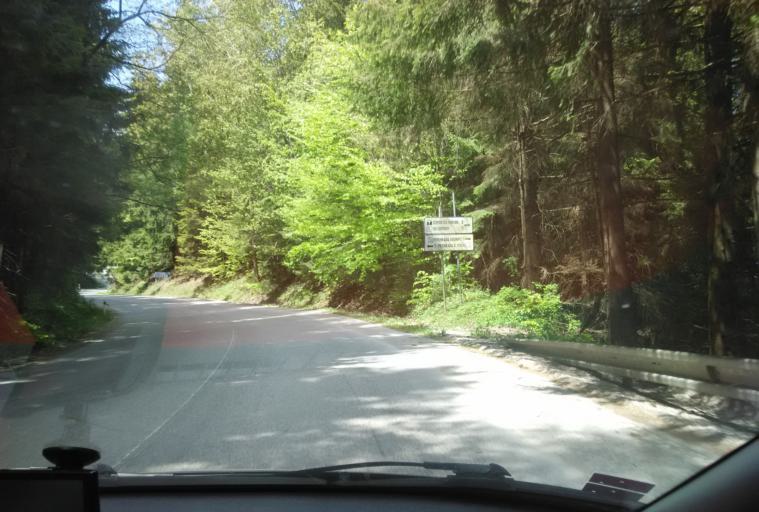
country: SK
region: Kosicky
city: Dobsina
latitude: 48.8559
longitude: 20.3809
